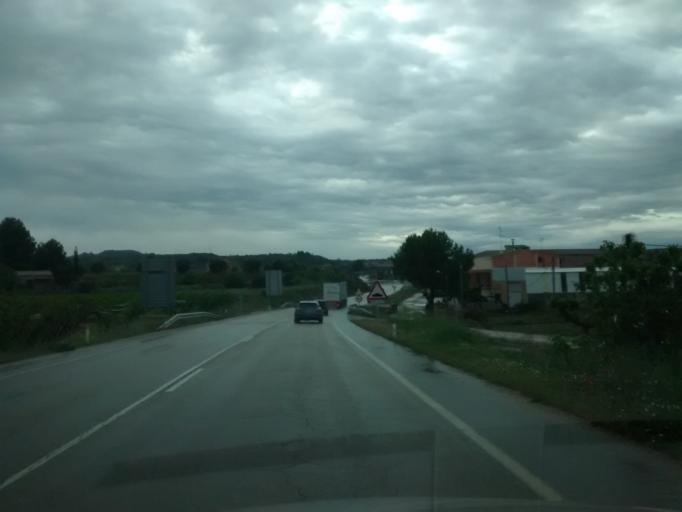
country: ES
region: Aragon
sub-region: Provincia de Zaragoza
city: Maella
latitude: 41.1272
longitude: 0.1331
